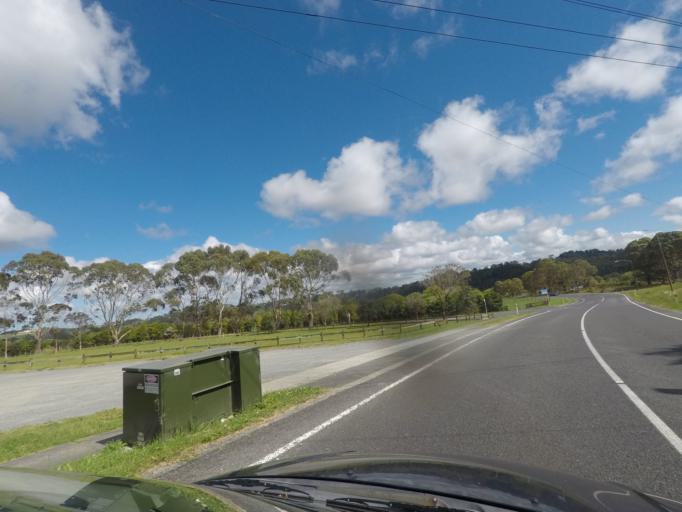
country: NZ
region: Auckland
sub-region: Auckland
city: Rothesay Bay
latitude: -36.7578
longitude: 174.6502
